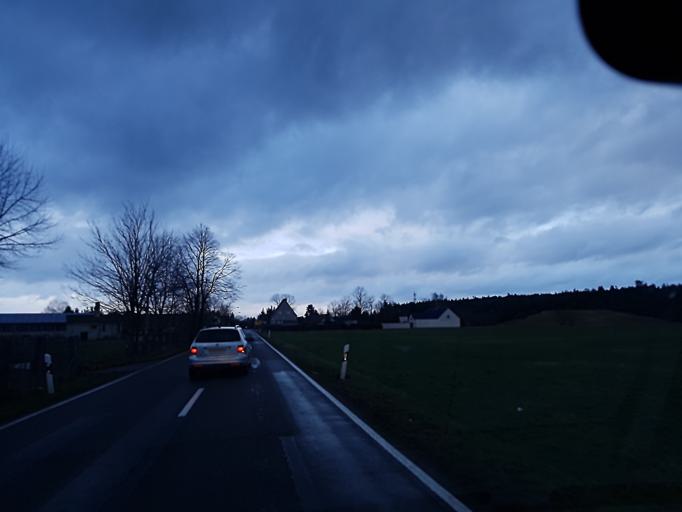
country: DE
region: Brandenburg
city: Finsterwalde
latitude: 51.5627
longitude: 13.6730
